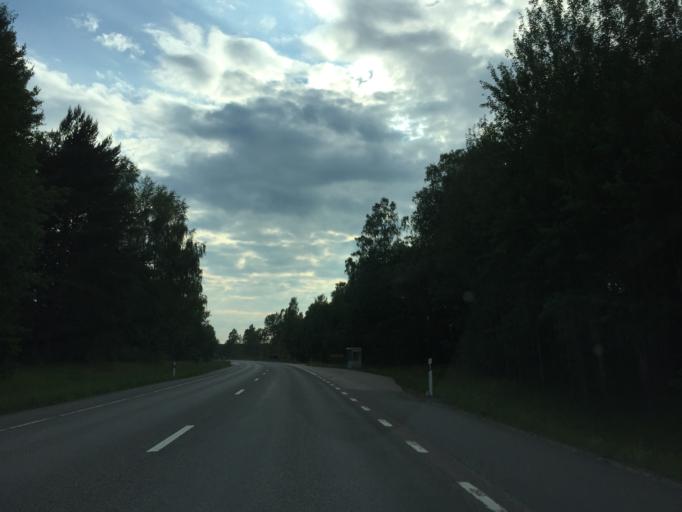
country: SE
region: OErebro
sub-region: Lindesbergs Kommun
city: Fellingsbro
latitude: 59.3452
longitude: 15.5976
